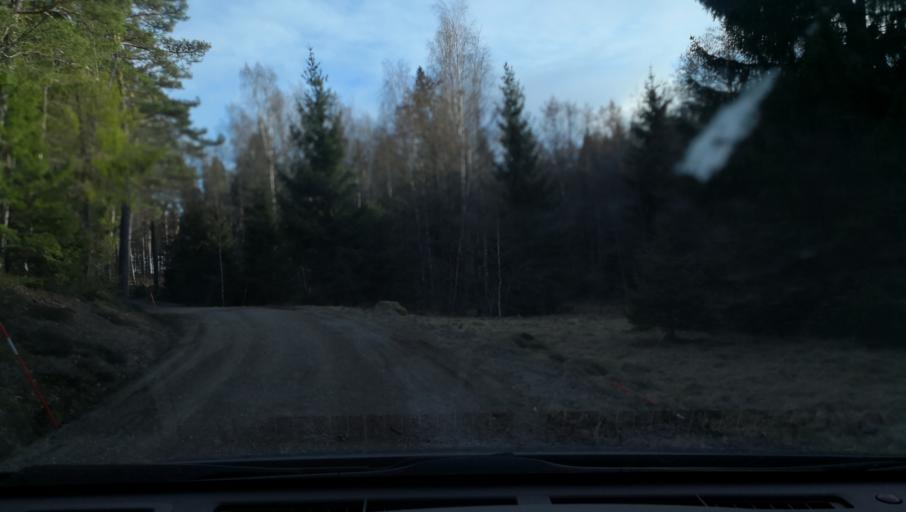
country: SE
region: Vaestmanland
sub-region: Arboga Kommun
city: Arboga
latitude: 59.4362
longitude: 15.7516
